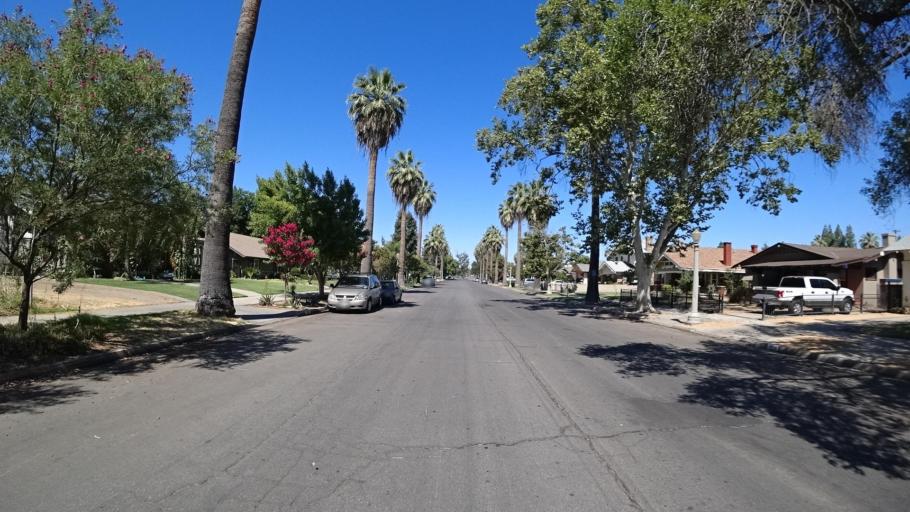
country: US
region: California
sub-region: Fresno County
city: Fresno
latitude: 36.7406
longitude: -119.7700
